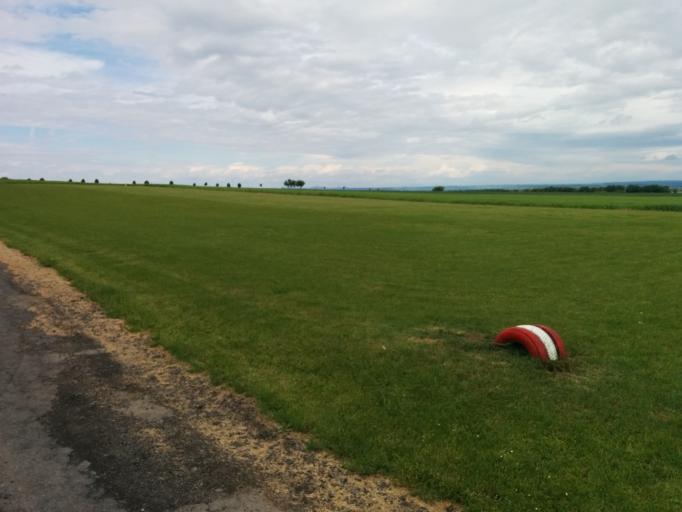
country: CZ
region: Central Bohemia
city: Libeznice
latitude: 50.1882
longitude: 14.4707
